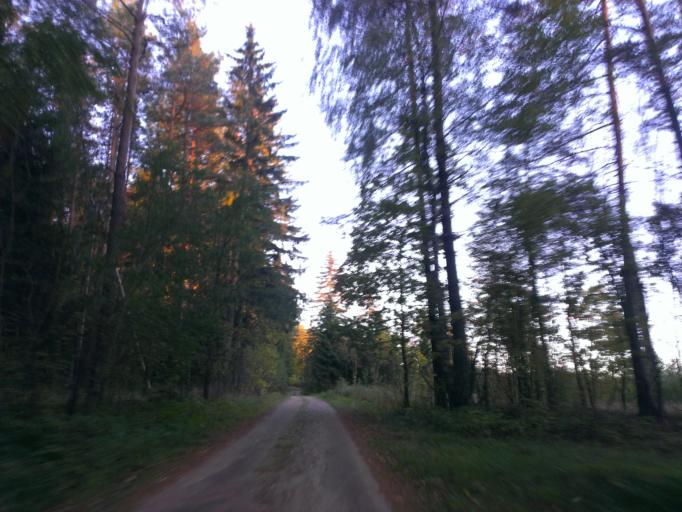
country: LV
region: Incukalns
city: Vangazi
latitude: 57.1238
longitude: 24.5683
